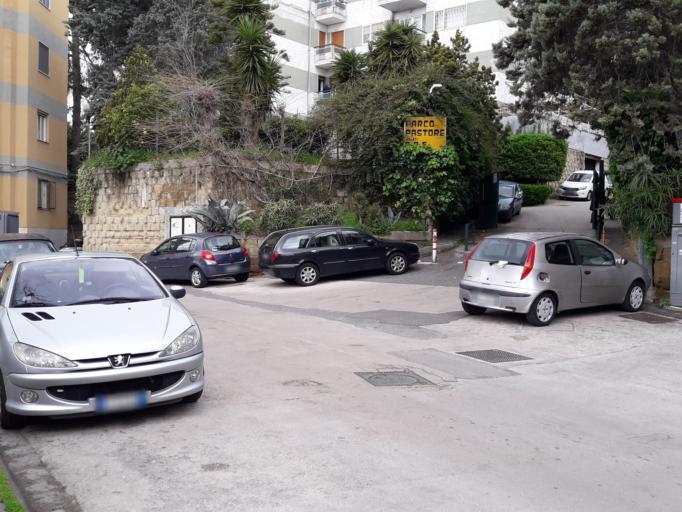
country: IT
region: Campania
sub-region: Provincia di Napoli
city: Napoli
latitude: 40.8580
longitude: 14.2246
